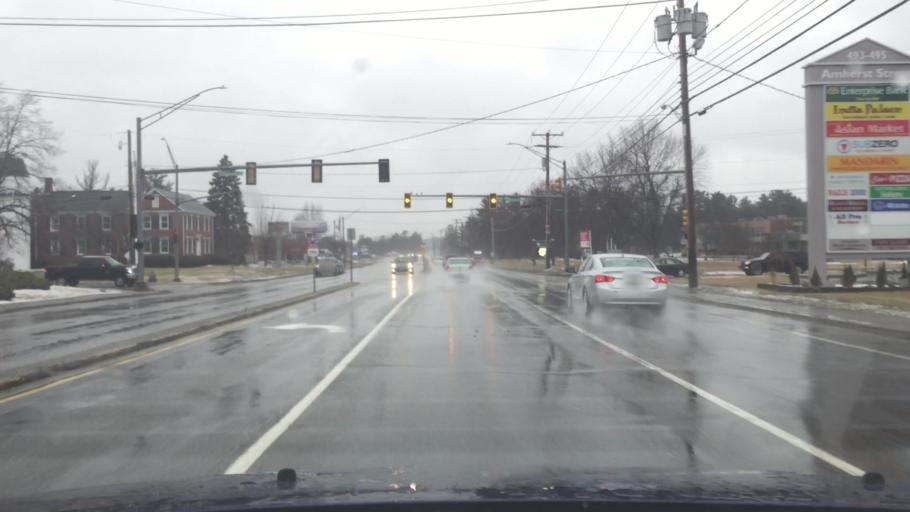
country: US
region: New Hampshire
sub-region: Hillsborough County
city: Nashua
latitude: 42.7928
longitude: -71.5226
